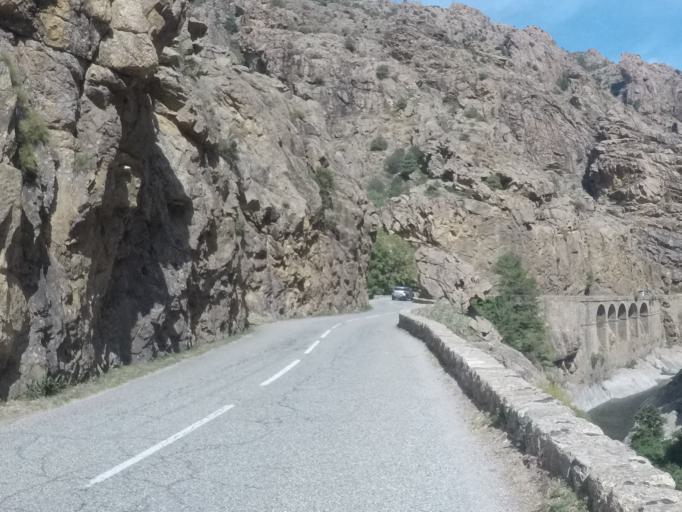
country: FR
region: Corsica
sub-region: Departement de la Haute-Corse
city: Corte
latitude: 42.3664
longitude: 9.0688
